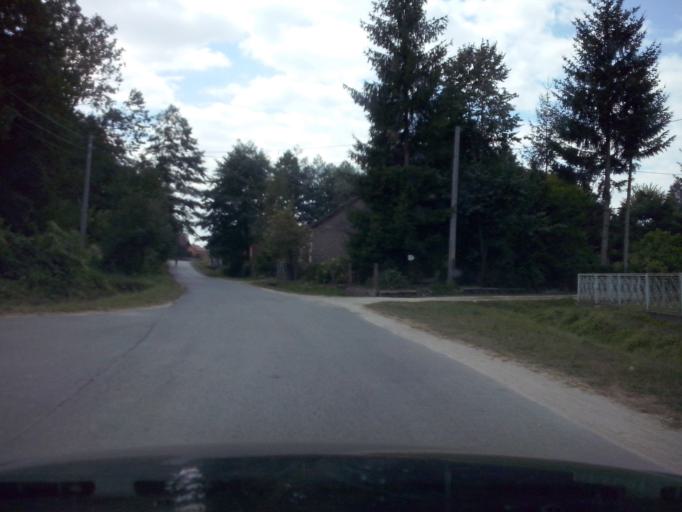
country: PL
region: Swietokrzyskie
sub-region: Powiat staszowski
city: Staszow
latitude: 50.5650
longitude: 21.1229
